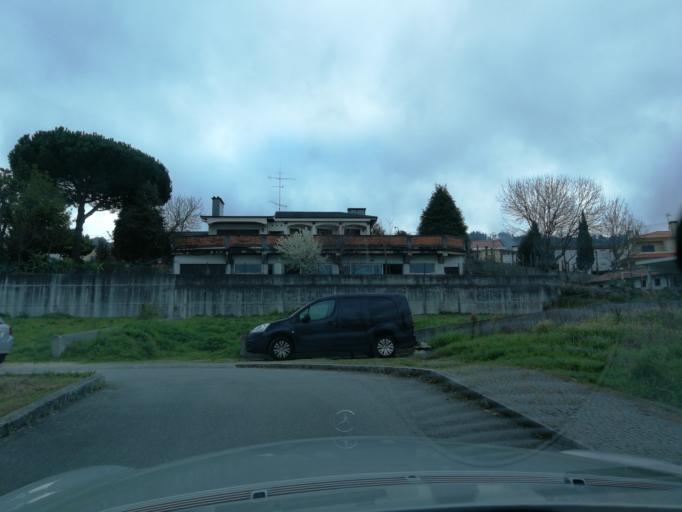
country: PT
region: Braga
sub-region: Braga
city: Braga
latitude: 41.5457
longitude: -8.3922
